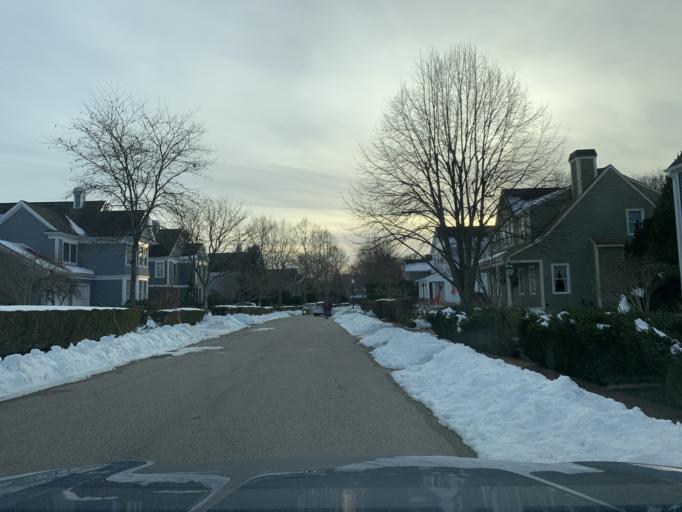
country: US
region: Rhode Island
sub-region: Washington County
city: North Kingstown
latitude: 41.5863
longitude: -71.4465
